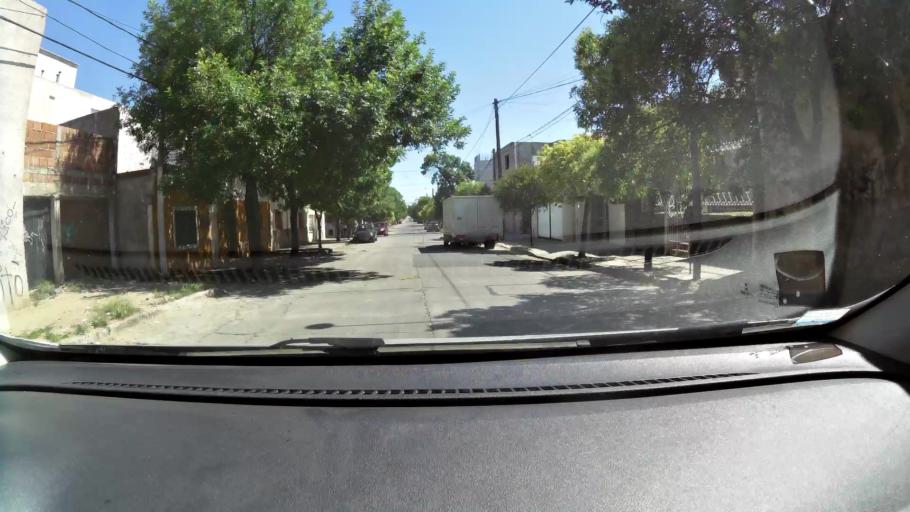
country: AR
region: Cordoba
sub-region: Departamento de Capital
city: Cordoba
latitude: -31.4229
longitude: -64.1391
